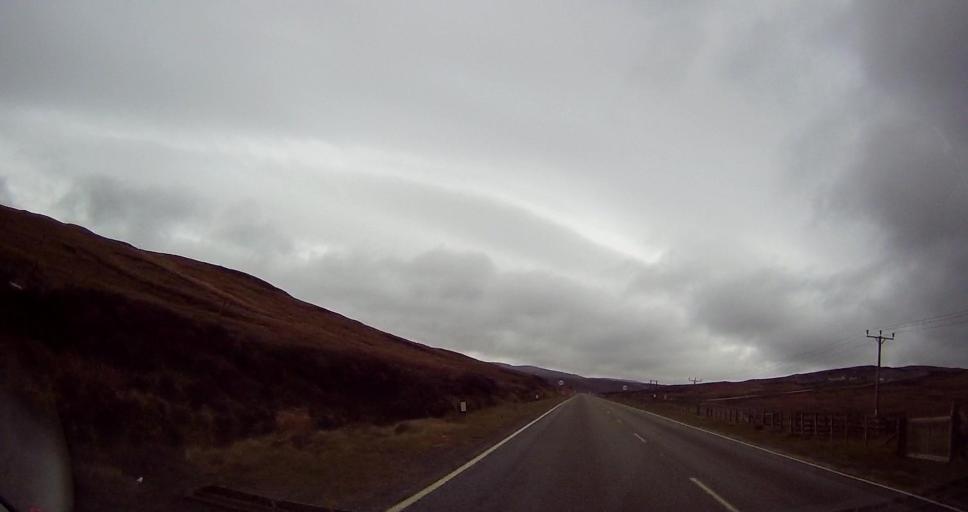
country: GB
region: Scotland
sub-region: Shetland Islands
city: Lerwick
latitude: 60.2700
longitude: -1.2348
